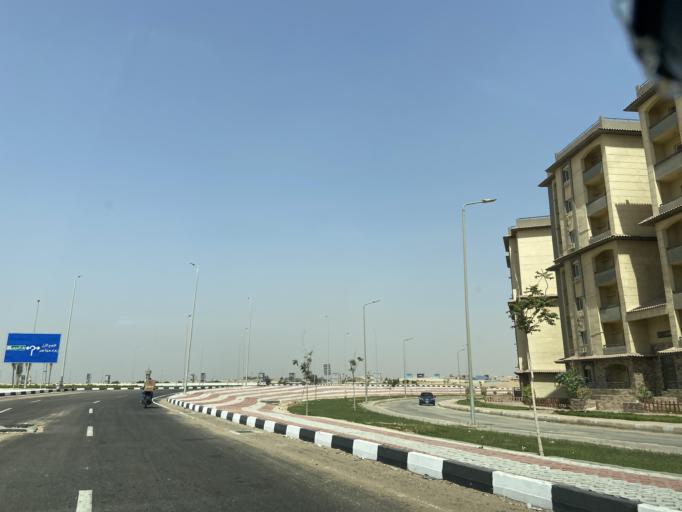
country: EG
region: Muhafazat al Qalyubiyah
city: Al Khankah
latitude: 30.0728
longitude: 31.3890
